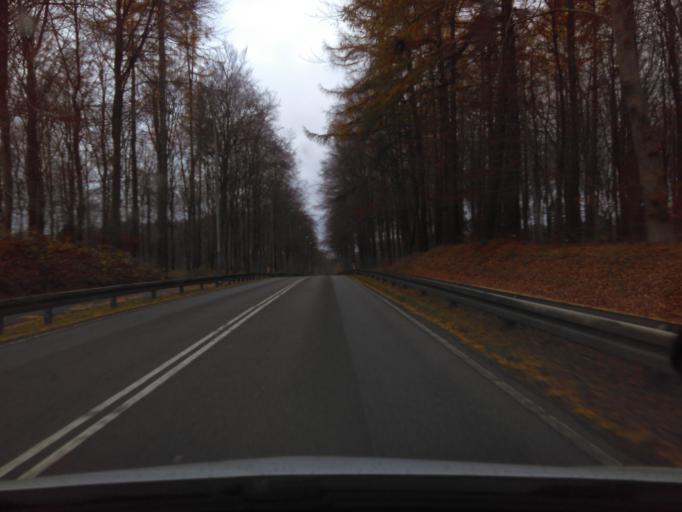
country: DK
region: Capital Region
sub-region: Fureso Kommune
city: Vaerlose
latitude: 55.7602
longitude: 12.3690
